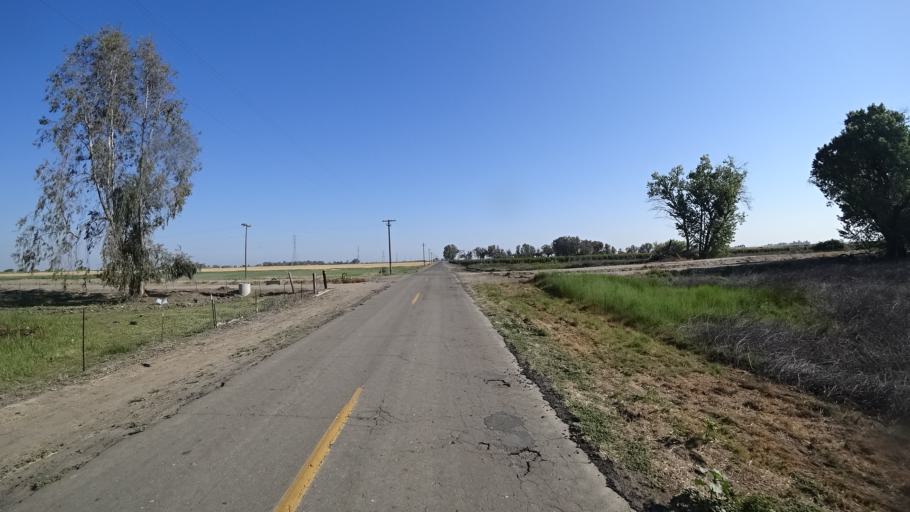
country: US
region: California
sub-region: Kings County
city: Lemoore Station
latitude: 36.3357
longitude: -119.8873
